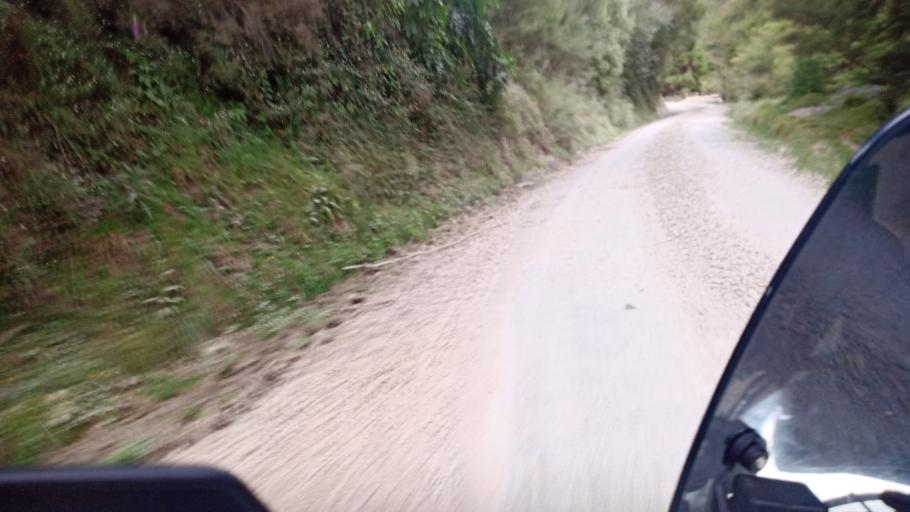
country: NZ
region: Gisborne
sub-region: Gisborne District
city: Gisborne
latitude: -38.4734
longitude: 177.9764
